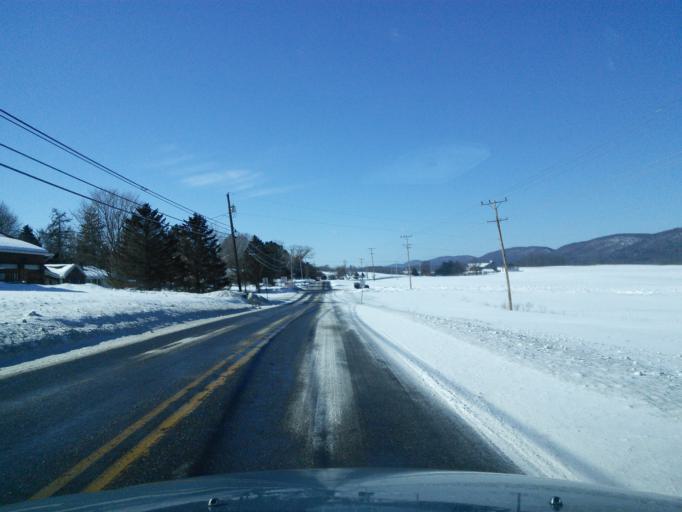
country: US
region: Pennsylvania
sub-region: Centre County
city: Bellefonte
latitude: 40.8925
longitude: -77.8147
